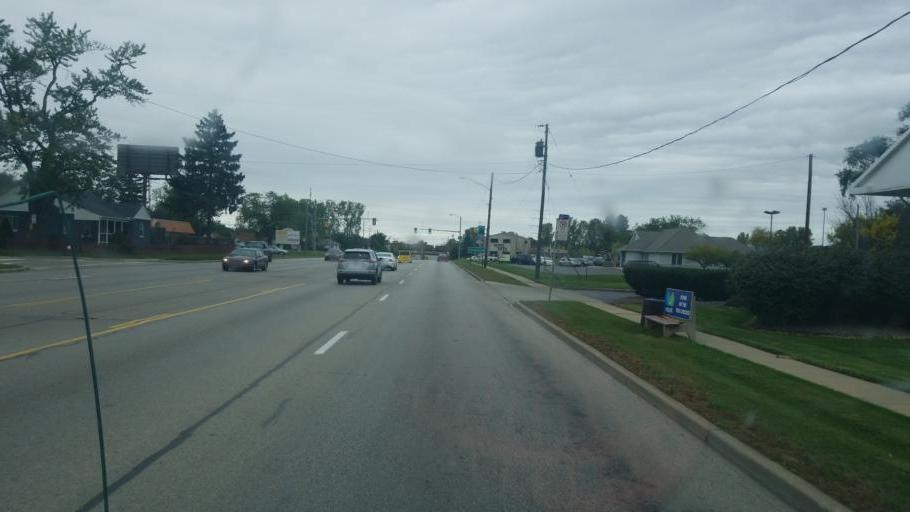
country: US
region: Ohio
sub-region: Lucas County
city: Holland
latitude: 41.6213
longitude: -83.6644
